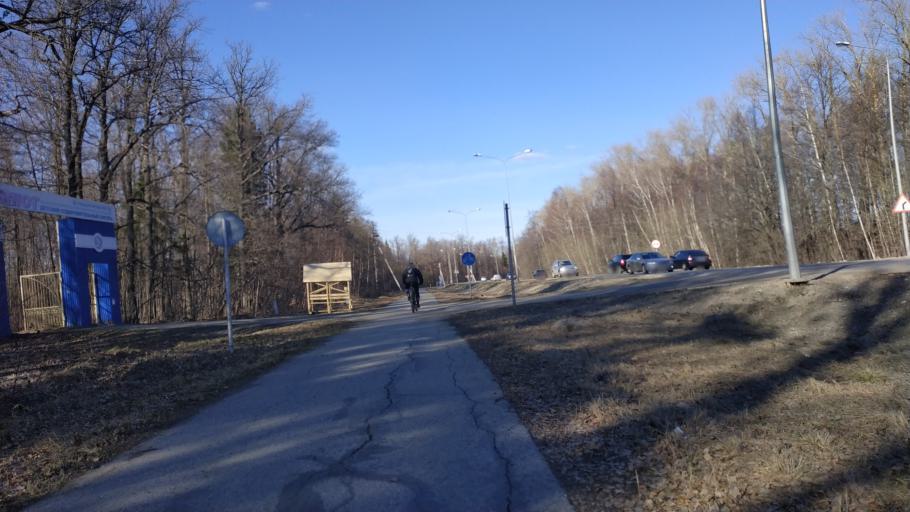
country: RU
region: Chuvashia
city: Ishley
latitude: 56.1295
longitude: 47.0711
